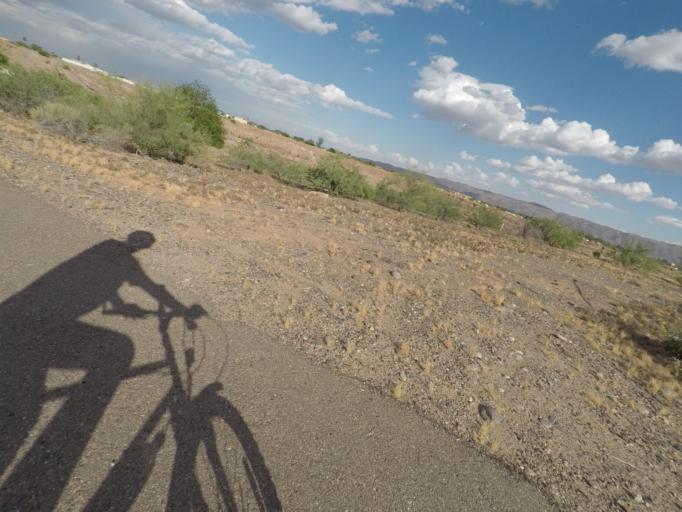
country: US
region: Arizona
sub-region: Maricopa County
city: Phoenix
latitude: 33.4128
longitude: -112.0909
